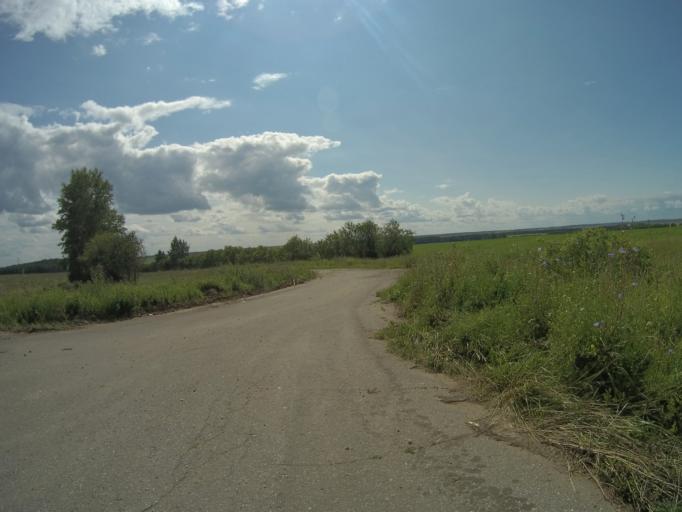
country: RU
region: Vladimir
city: Vladimir
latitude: 56.2381
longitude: 40.3811
